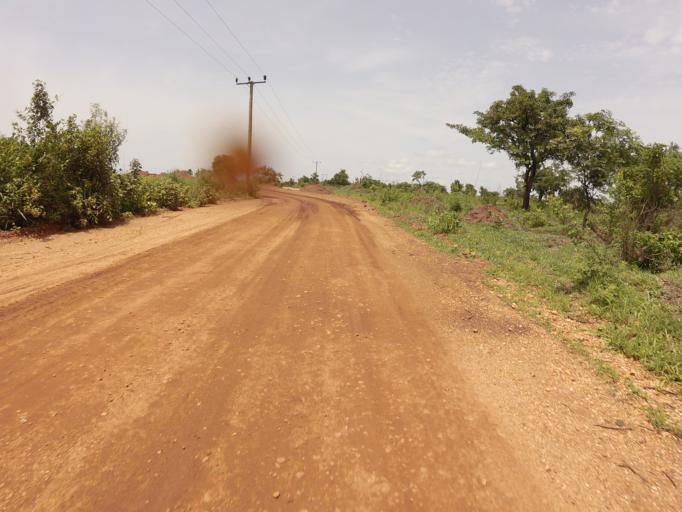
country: GH
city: Kpandae
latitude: 8.7127
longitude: 0.1472
